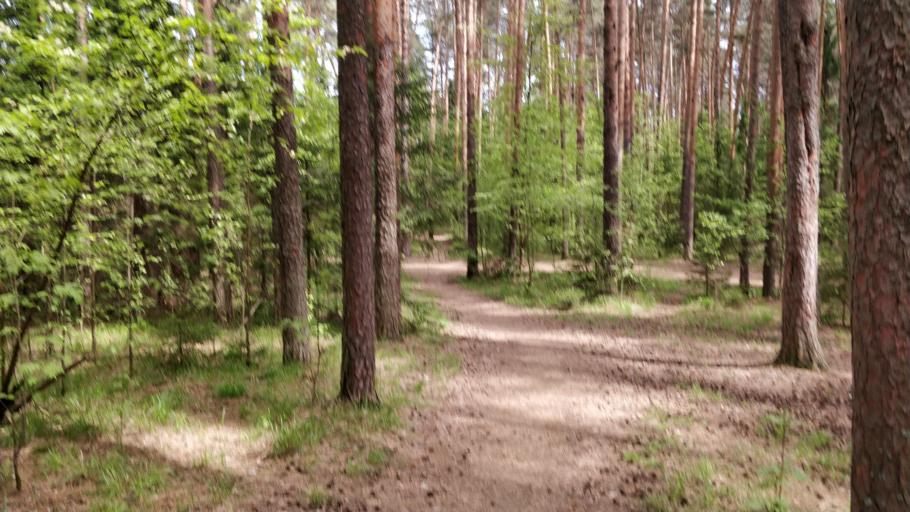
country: RU
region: Perm
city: Kondratovo
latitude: 57.9839
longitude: 56.1460
